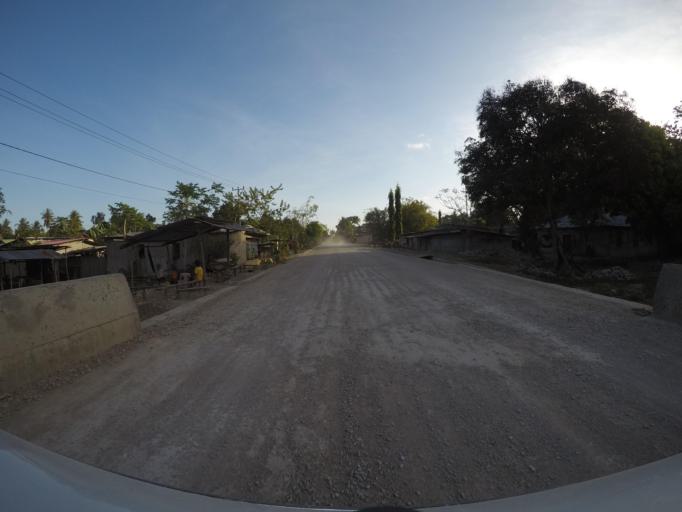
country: TL
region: Viqueque
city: Viqueque
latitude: -8.8244
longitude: 126.5300
